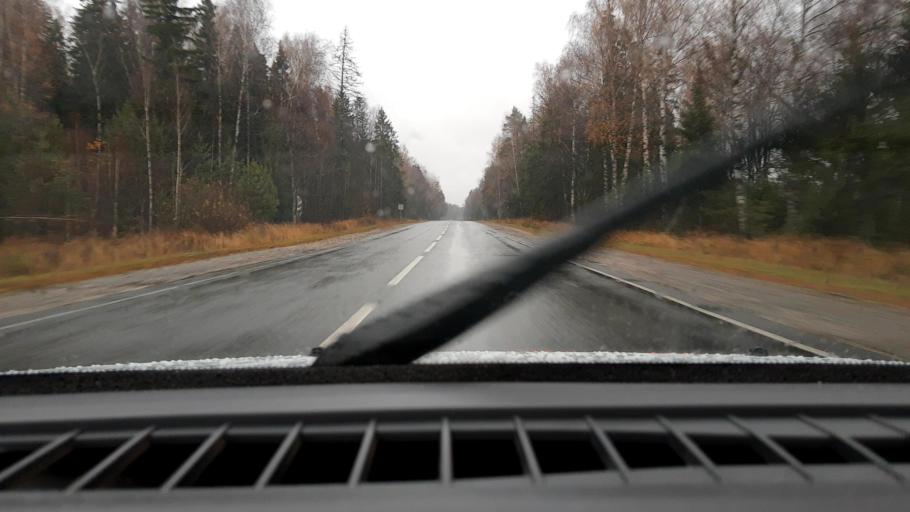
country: RU
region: Nizjnij Novgorod
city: Linda
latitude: 56.6270
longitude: 44.0844
